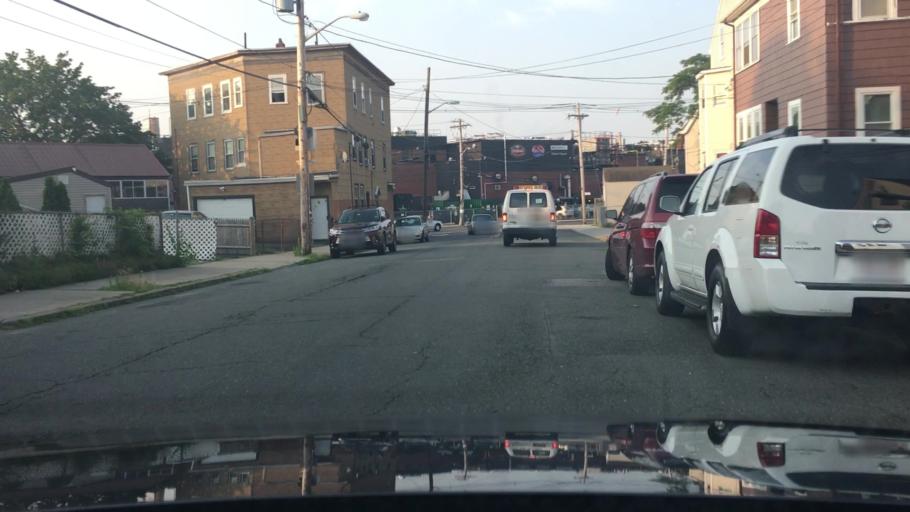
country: US
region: Massachusetts
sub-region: Essex County
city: Lynn
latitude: 42.4663
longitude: -70.9695
